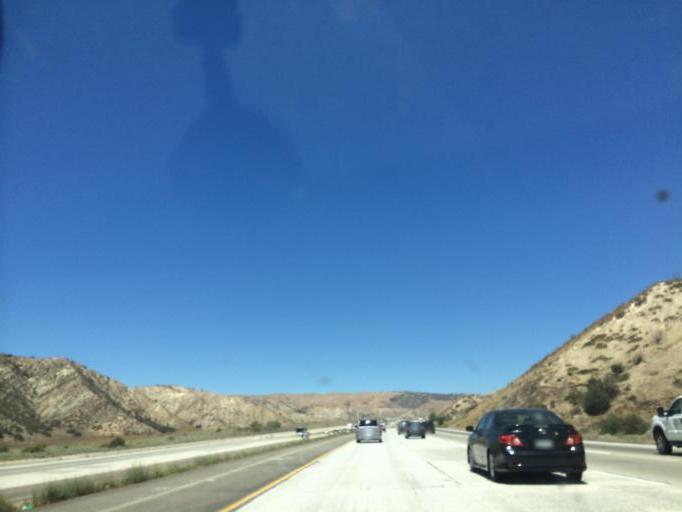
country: US
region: California
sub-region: Kern County
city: Lebec
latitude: 34.7270
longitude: -118.7990
